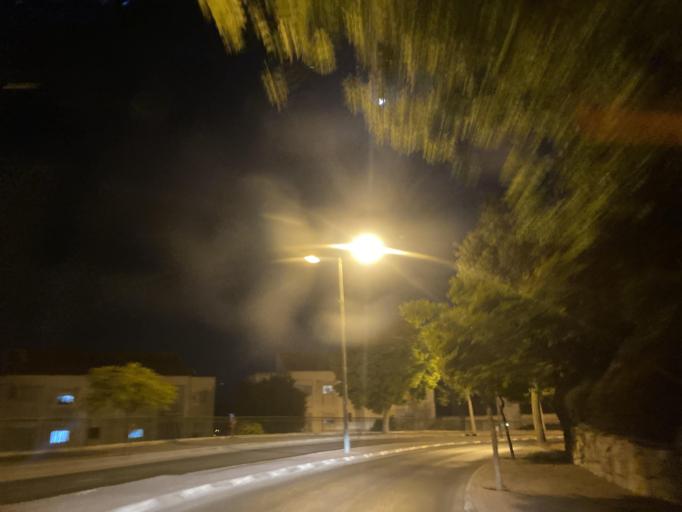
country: IL
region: Haifa
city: Daliyat el Karmil
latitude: 32.6431
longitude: 35.0899
